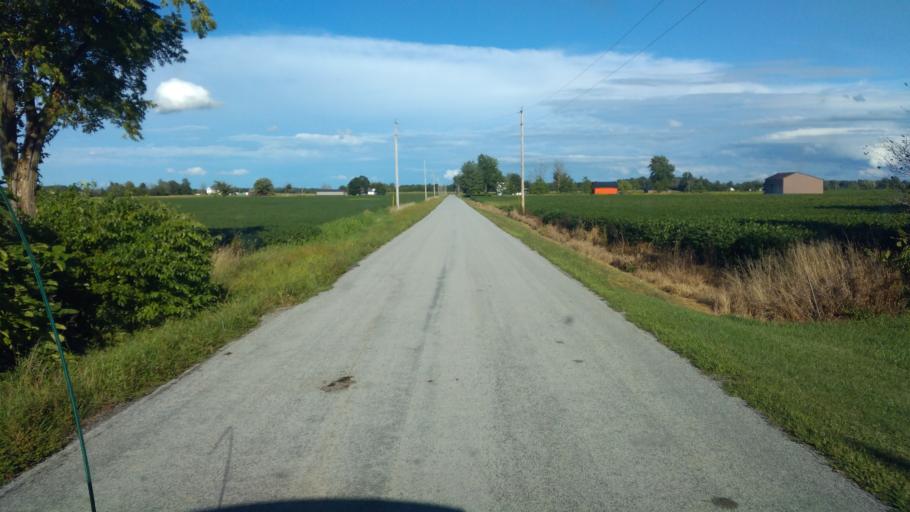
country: US
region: Ohio
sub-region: Hardin County
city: Forest
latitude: 40.7606
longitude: -83.6144
